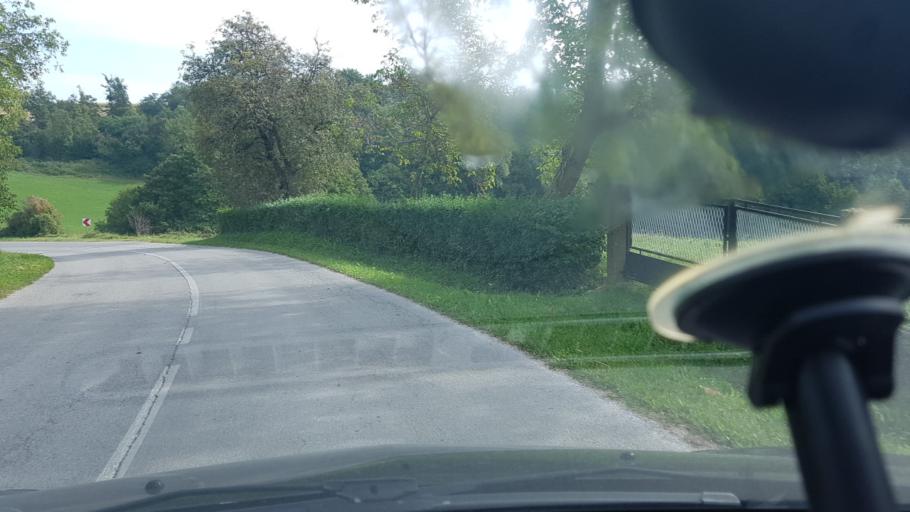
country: HR
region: Varazdinska
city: Ljubescica
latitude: 46.0970
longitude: 16.3436
